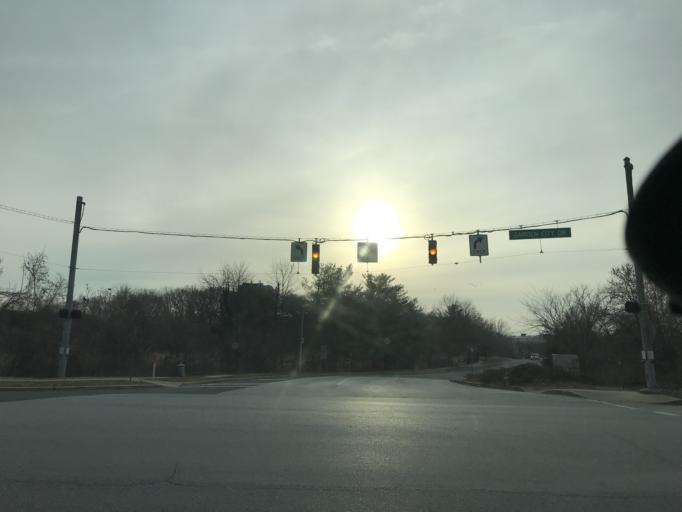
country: US
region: Maryland
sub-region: Prince George's County
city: Lanham
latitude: 38.9482
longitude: -76.8693
